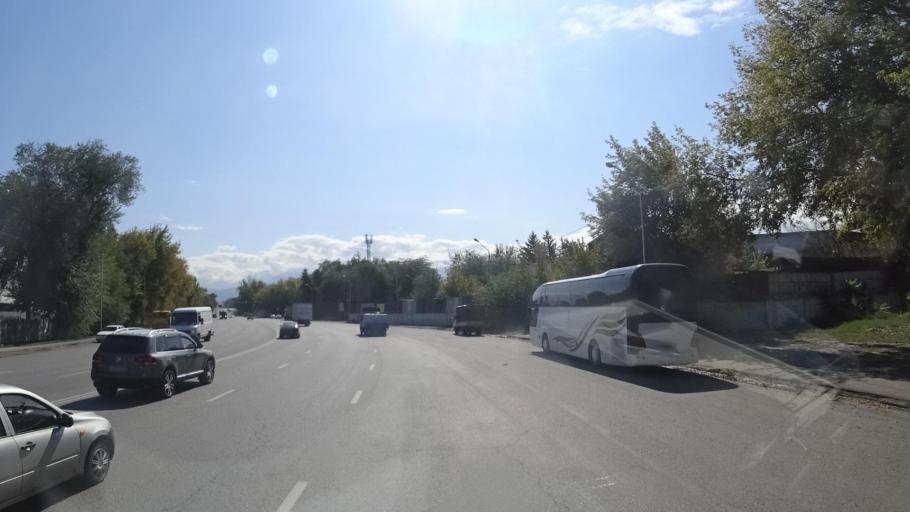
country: KZ
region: Almaty Oblysy
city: Pervomayskiy
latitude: 43.3450
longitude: 76.9712
